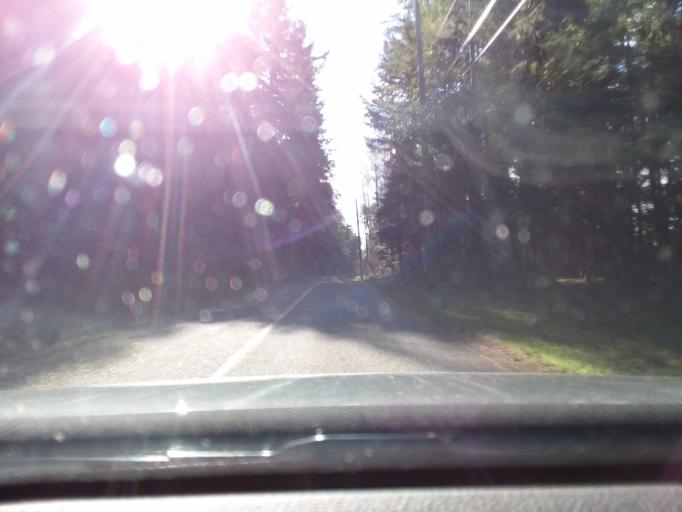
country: CA
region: British Columbia
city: North Cowichan
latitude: 48.9593
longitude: -123.5440
